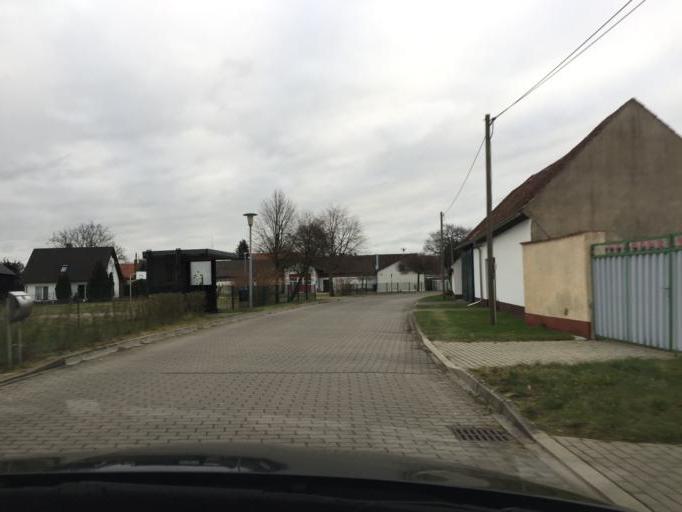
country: DE
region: Brandenburg
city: Vetschau
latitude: 51.7993
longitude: 14.0890
